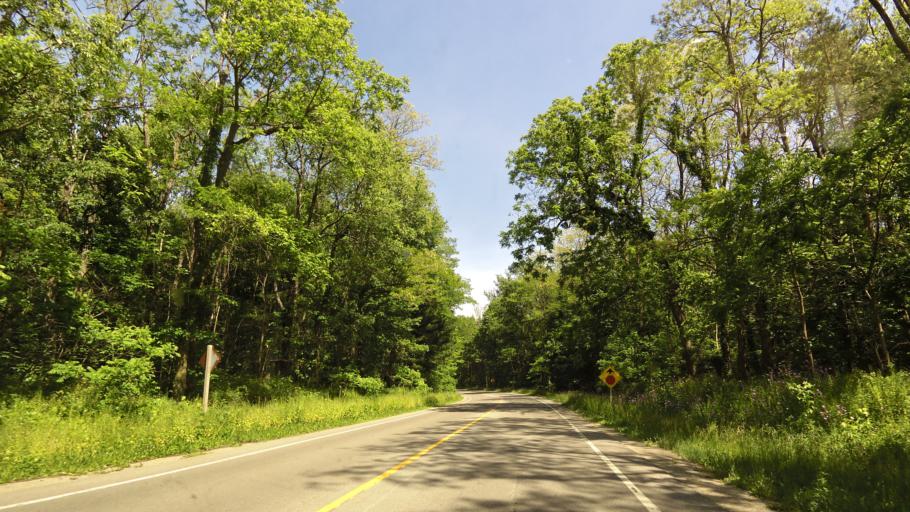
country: CA
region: Ontario
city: Norfolk County
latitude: 42.6979
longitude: -80.3387
